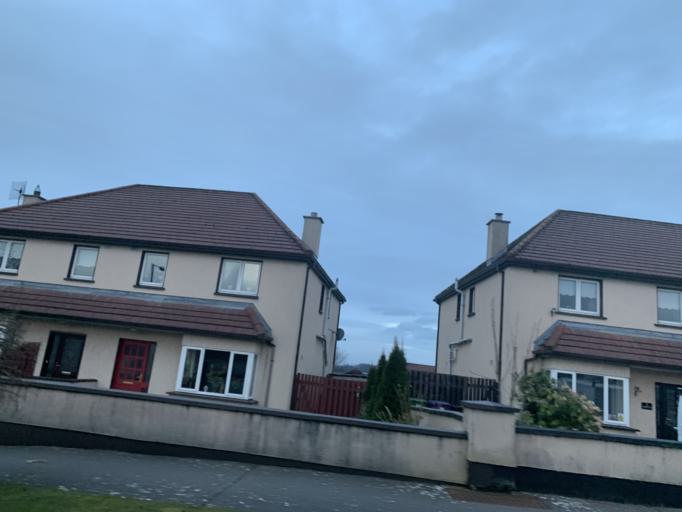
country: IE
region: Connaught
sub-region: Sligo
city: Collooney
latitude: 54.1798
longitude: -8.4921
